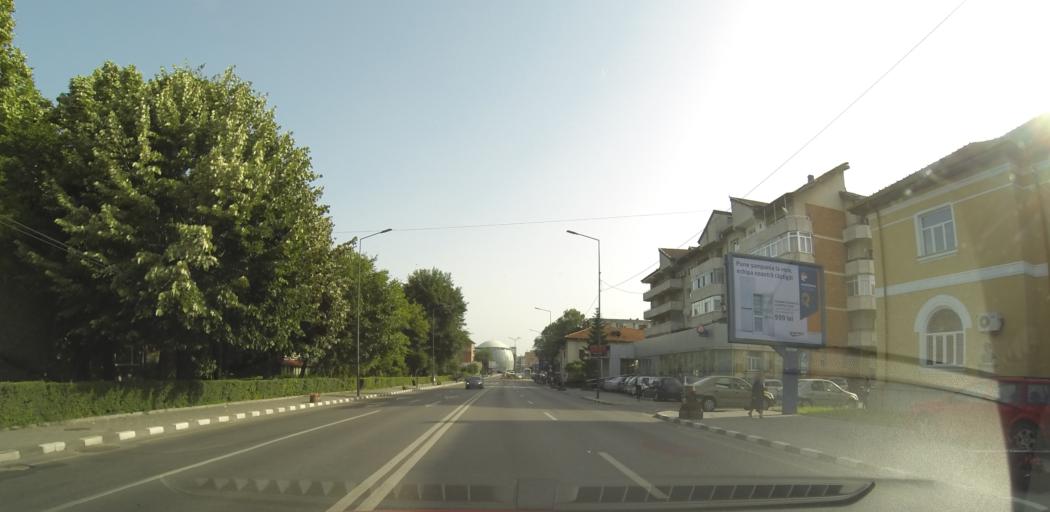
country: RO
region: Valcea
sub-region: Municipiul Ramnicu Valcea
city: Ramnicu Valcea
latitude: 45.0979
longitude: 24.3619
